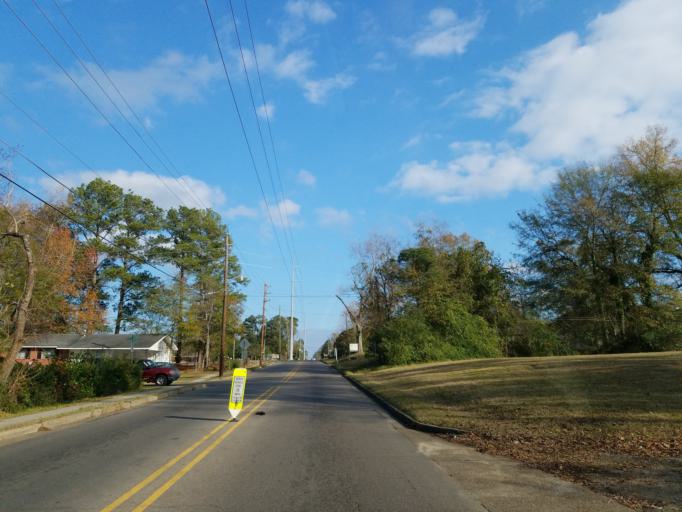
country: US
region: Mississippi
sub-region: Forrest County
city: Glendale
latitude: 31.3357
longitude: -89.3268
